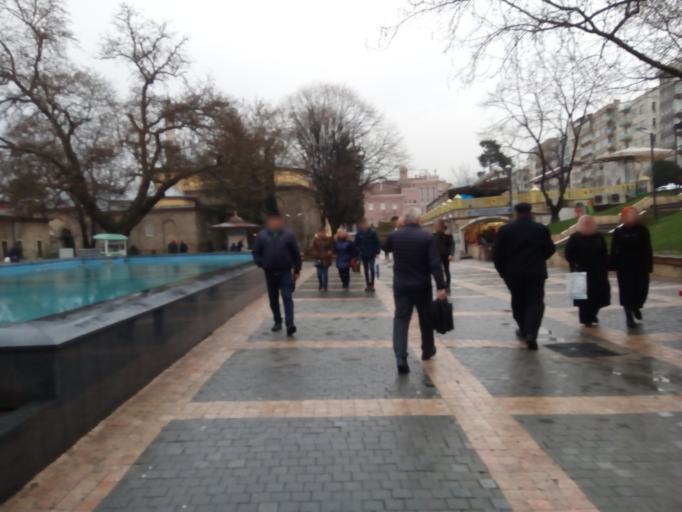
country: TR
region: Bursa
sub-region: Osmangazi
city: Bursa
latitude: 40.1838
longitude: 29.0631
